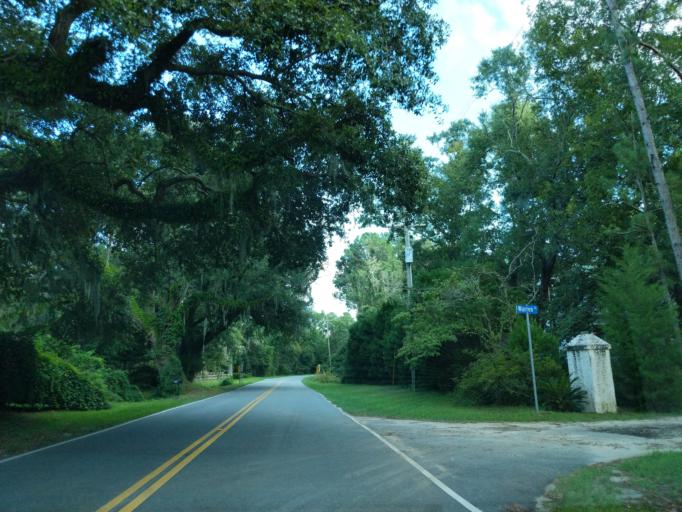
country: US
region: South Carolina
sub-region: Charleston County
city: Awendaw
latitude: 33.0970
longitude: -79.4670
